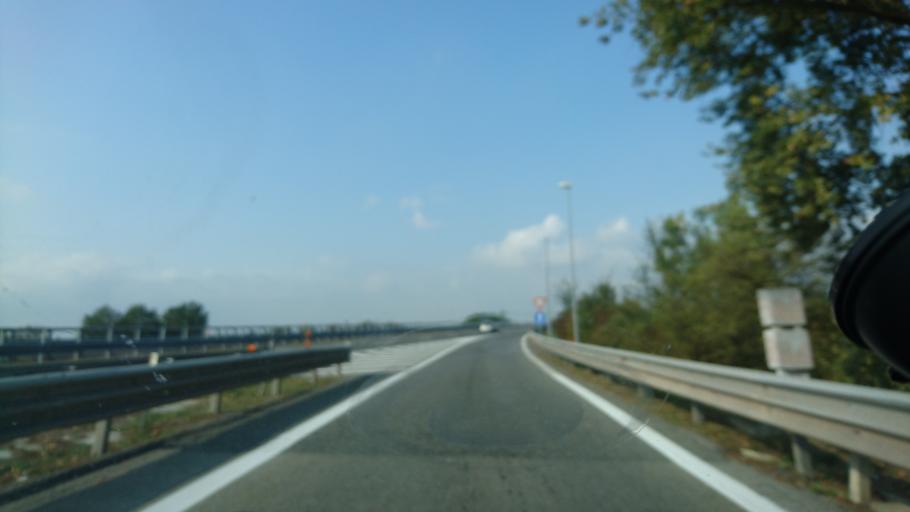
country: IT
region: Piedmont
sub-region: Provincia di Alessandria
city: Castellazzo Bormida
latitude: 44.8746
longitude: 8.5723
